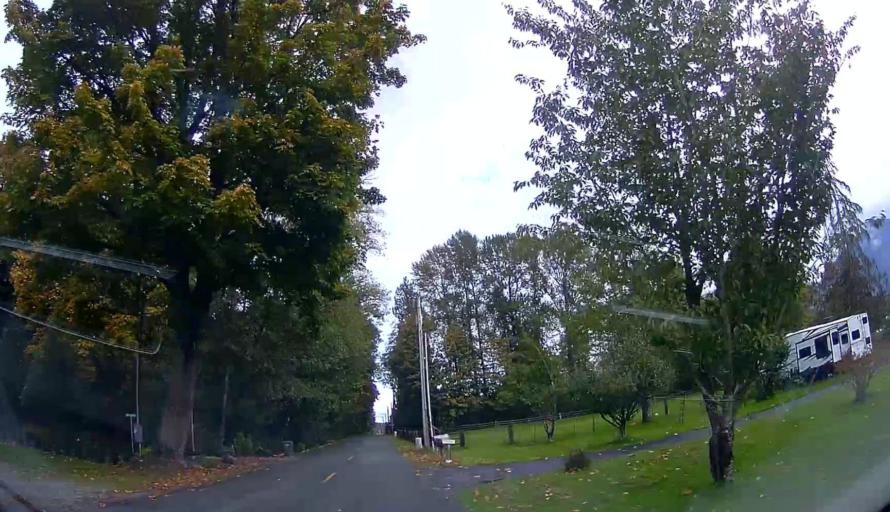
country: US
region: Washington
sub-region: Skagit County
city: Sedro-Woolley
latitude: 48.5338
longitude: -122.0251
